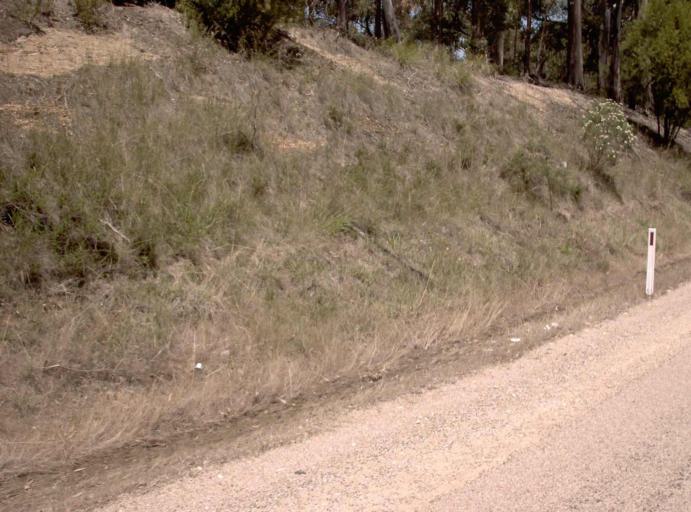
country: AU
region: Victoria
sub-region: East Gippsland
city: Bairnsdale
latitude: -37.7395
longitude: 147.7665
